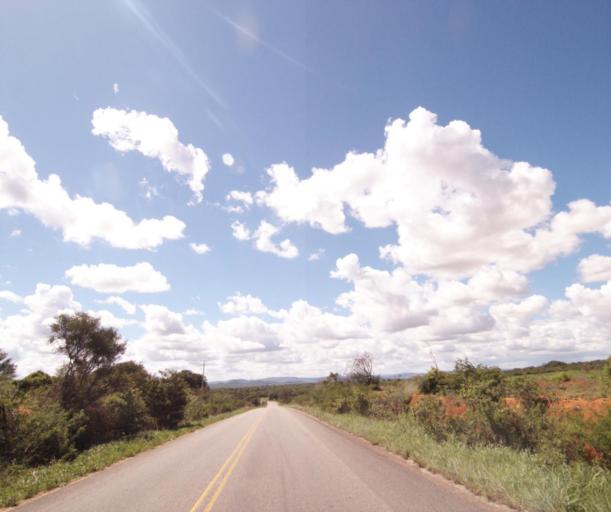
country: BR
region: Bahia
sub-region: Cacule
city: Cacule
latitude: -14.1819
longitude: -42.1656
